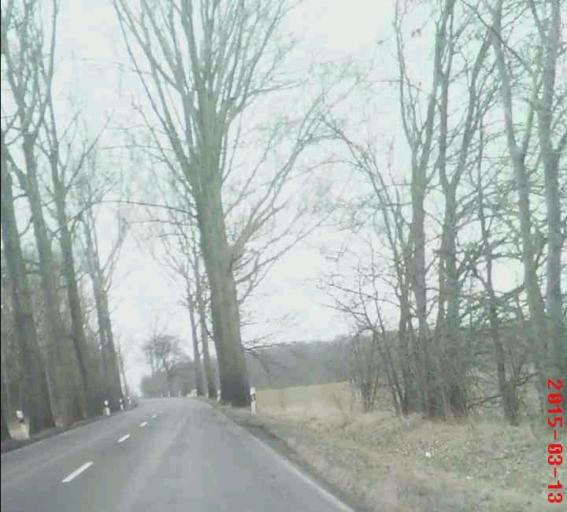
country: DE
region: Thuringia
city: Schonstedt
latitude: 51.0690
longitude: 10.5911
